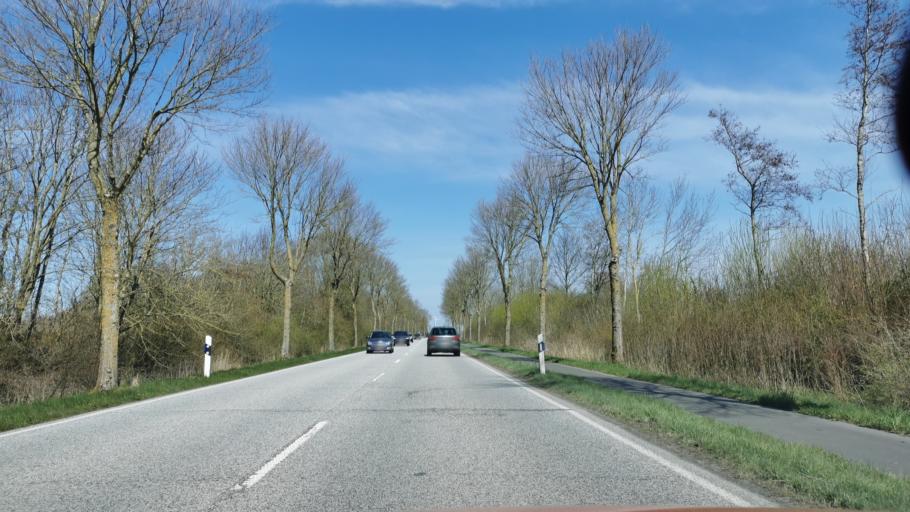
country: DE
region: Schleswig-Holstein
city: Wohrden
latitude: 54.1655
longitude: 8.9752
